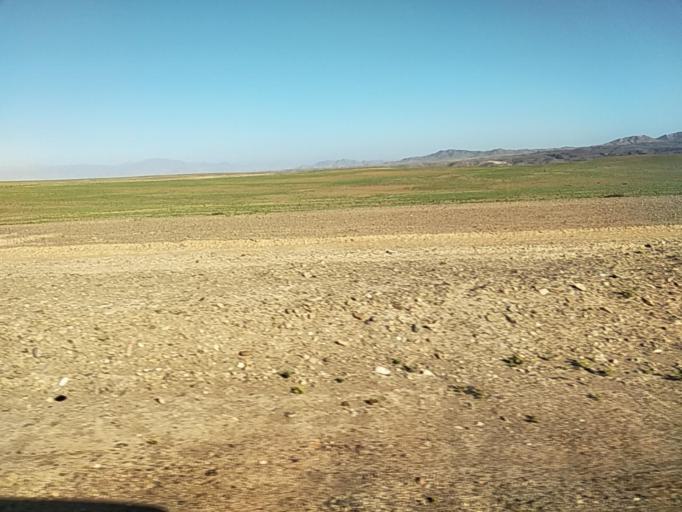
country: CL
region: Atacama
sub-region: Provincia de Copiapo
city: Copiapo
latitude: -27.3274
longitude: -70.7642
